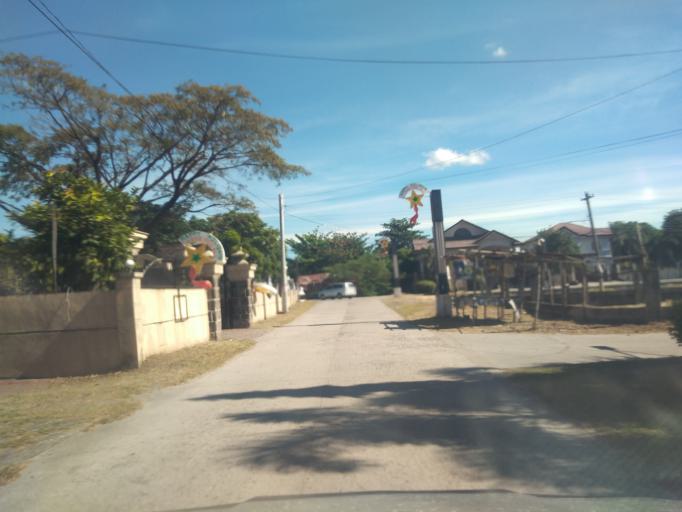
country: PH
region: Central Luzon
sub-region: Province of Pampanga
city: Bacolor
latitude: 15.0001
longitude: 120.6488
